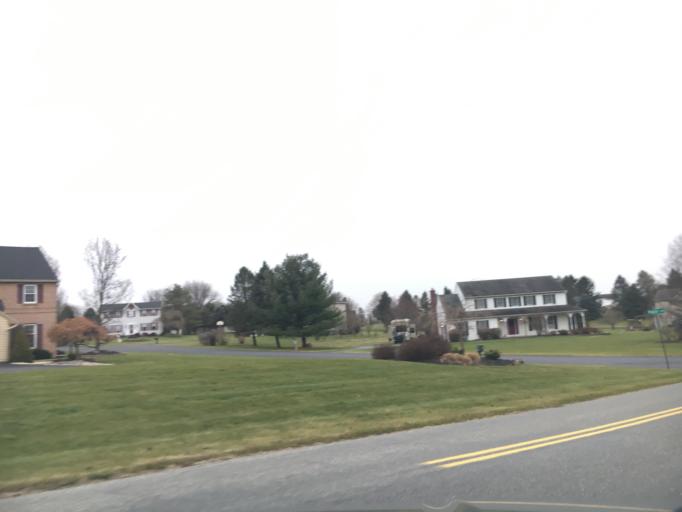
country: US
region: Pennsylvania
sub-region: Lehigh County
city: Schnecksville
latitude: 40.6862
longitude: -75.5831
